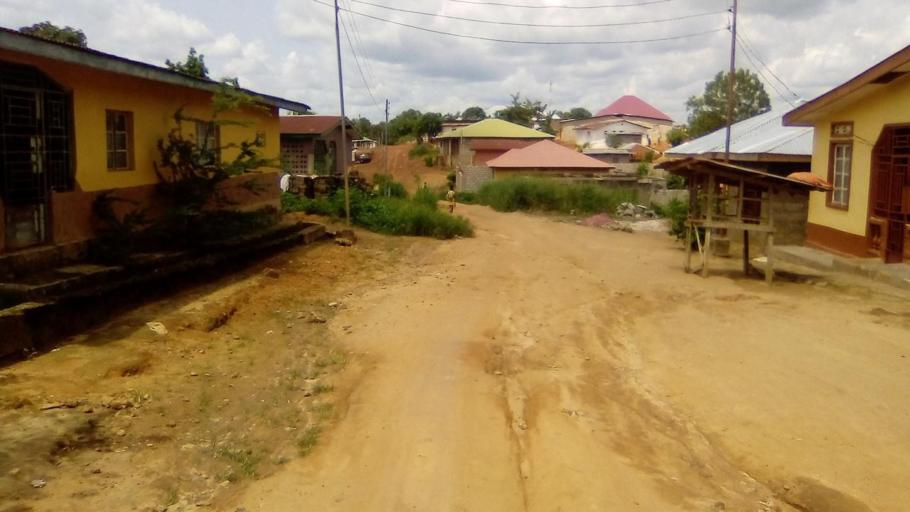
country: SL
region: Southern Province
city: Bo
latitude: 7.9667
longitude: -11.7221
